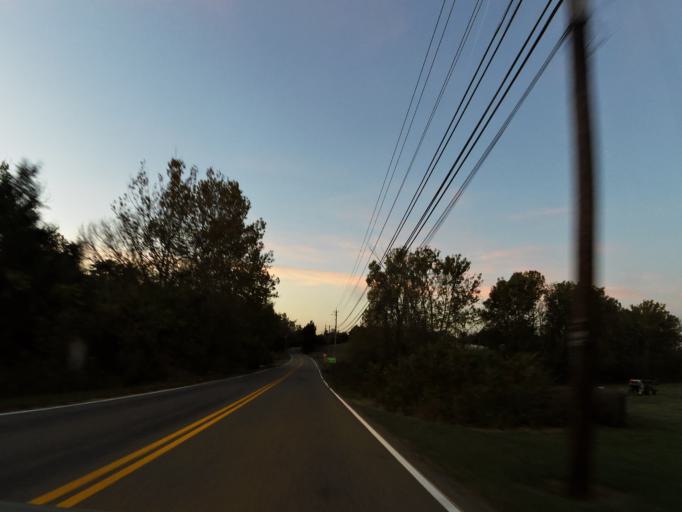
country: US
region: Tennessee
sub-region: Knox County
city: Mascot
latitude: 35.9894
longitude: -83.6324
